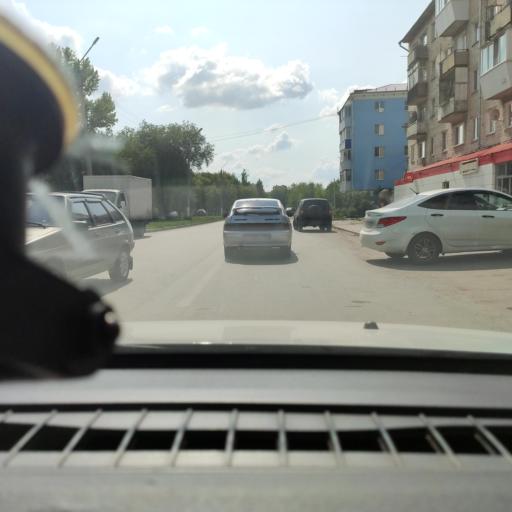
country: RU
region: Samara
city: Chapayevsk
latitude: 52.9905
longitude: 49.7097
